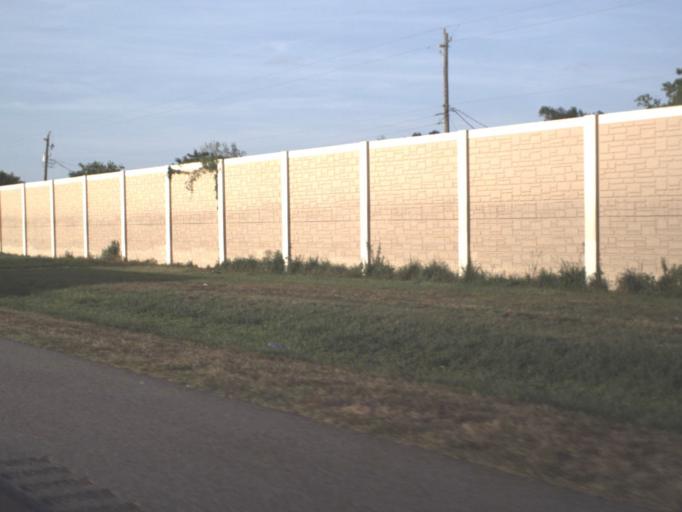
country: US
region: Florida
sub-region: Brevard County
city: Titusville
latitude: 28.5864
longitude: -80.8512
